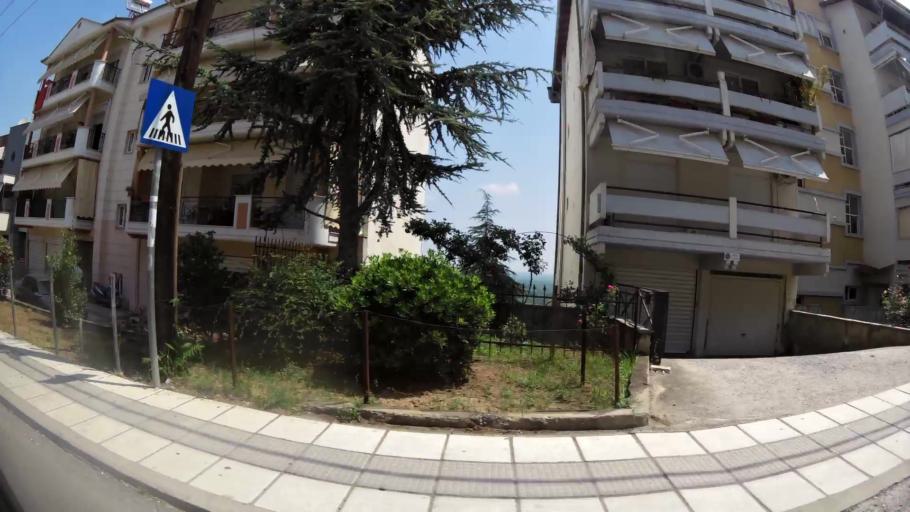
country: GR
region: Central Macedonia
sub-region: Nomos Imathias
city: Veroia
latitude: 40.5142
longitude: 22.2043
